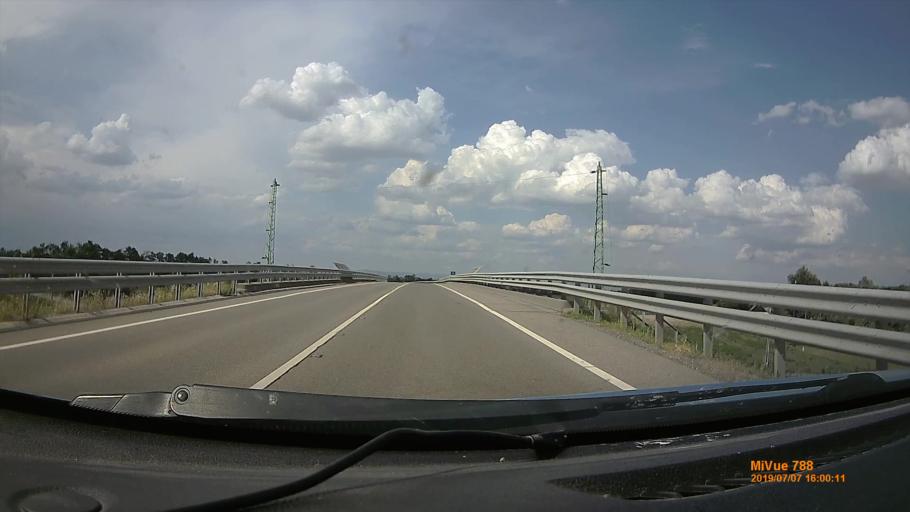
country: HU
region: Heves
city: Boldog
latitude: 47.5959
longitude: 19.7493
